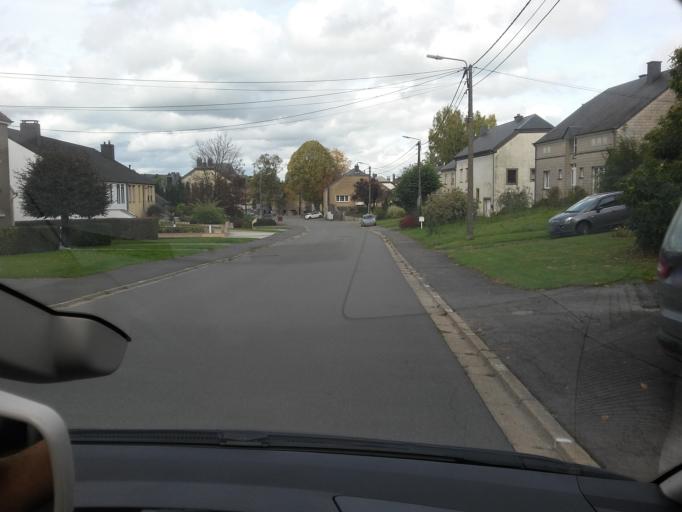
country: BE
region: Wallonia
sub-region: Province du Luxembourg
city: Arlon
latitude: 49.6829
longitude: 5.7708
